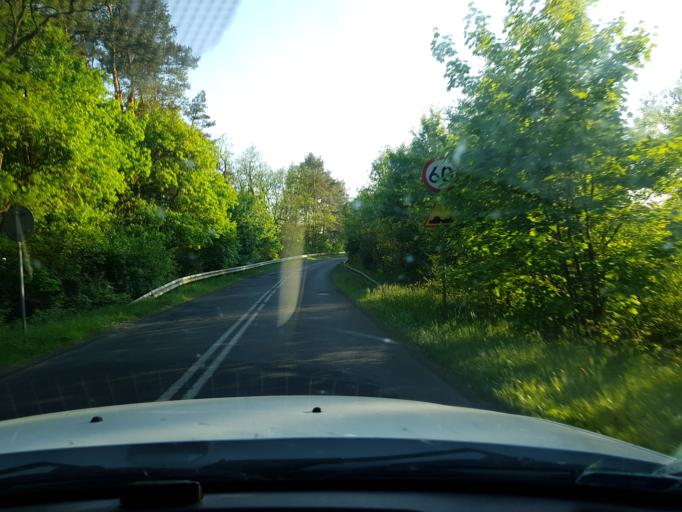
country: PL
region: West Pomeranian Voivodeship
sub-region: Powiat stargardzki
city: Kobylanka
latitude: 53.4358
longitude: 14.9089
